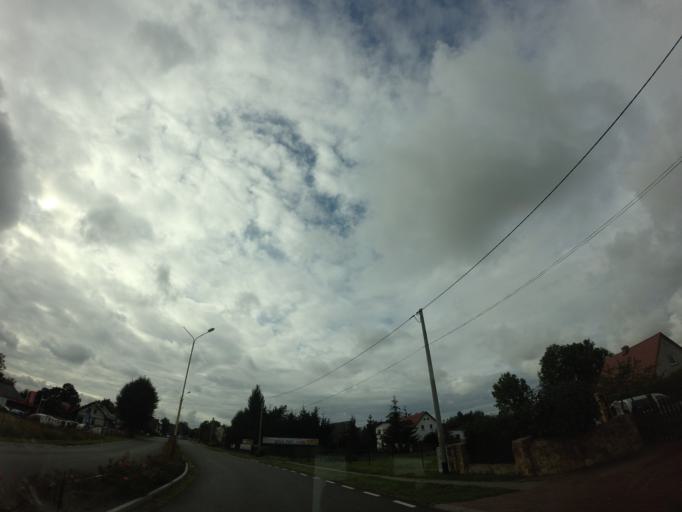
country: PL
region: West Pomeranian Voivodeship
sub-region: Powiat goleniowski
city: Stepnica
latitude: 53.6524
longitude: 14.6432
